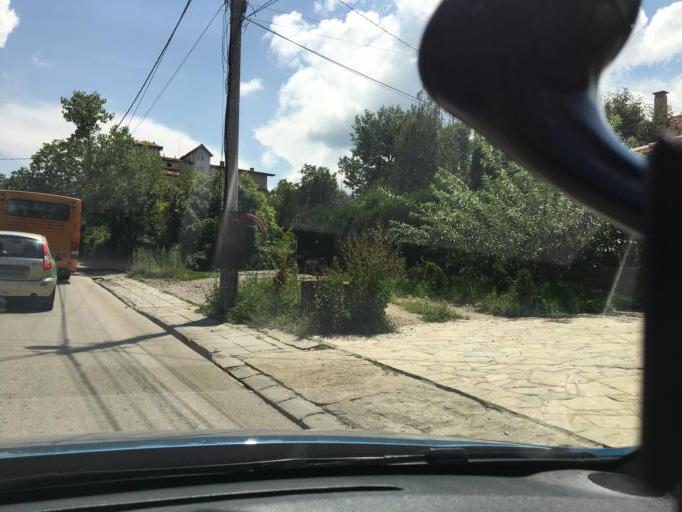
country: BG
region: Sofia-Capital
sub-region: Stolichna Obshtina
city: Sofia
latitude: 42.6199
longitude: 23.3350
